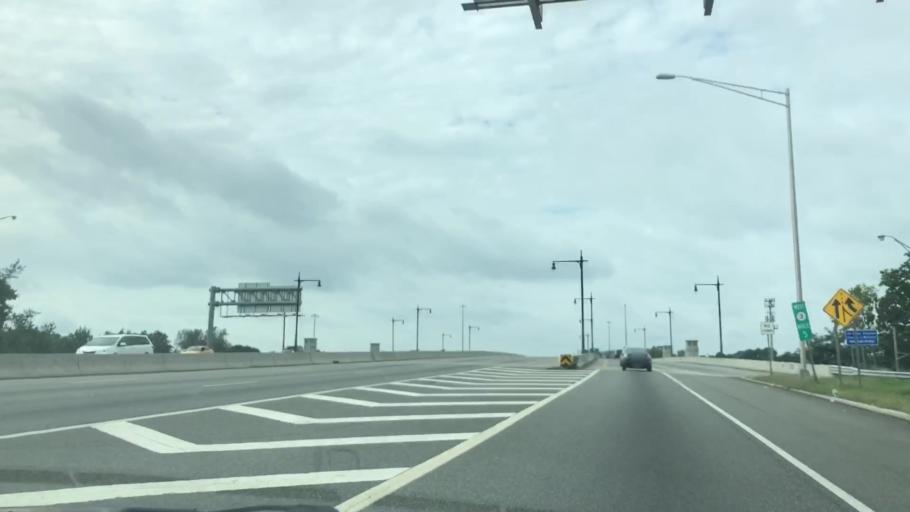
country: US
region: New Jersey
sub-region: Bergen County
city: Lyndhurst
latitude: 40.8222
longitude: -74.1223
